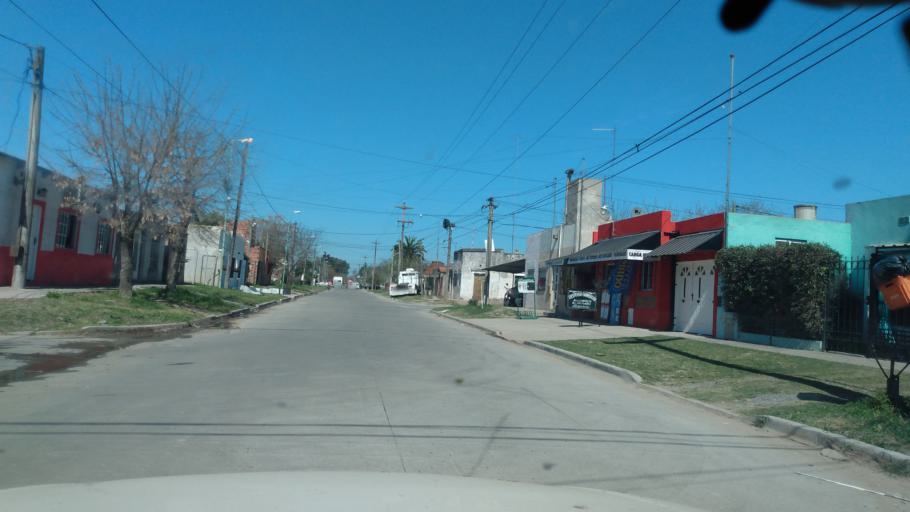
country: AR
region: Buenos Aires
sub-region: Partido de Lujan
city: Lujan
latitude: -34.5786
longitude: -59.1254
